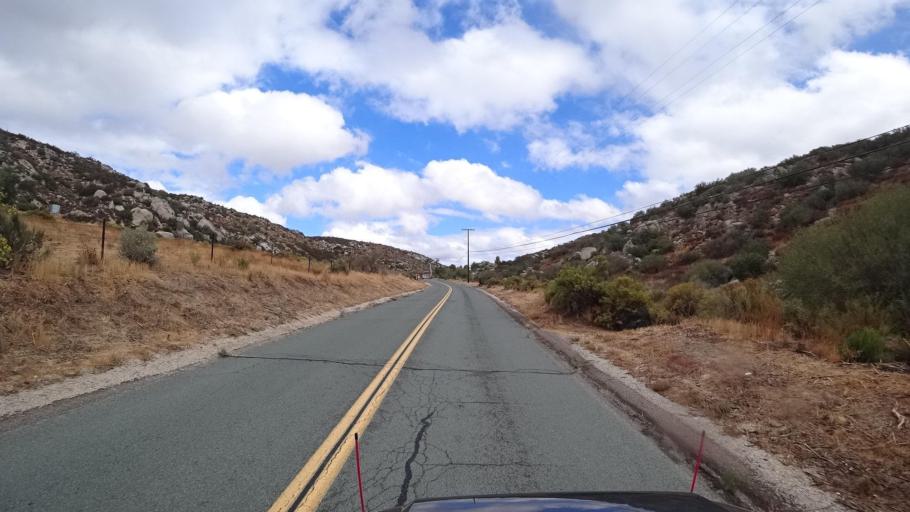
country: US
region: California
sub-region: San Diego County
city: Campo
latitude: 32.7006
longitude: -116.4325
